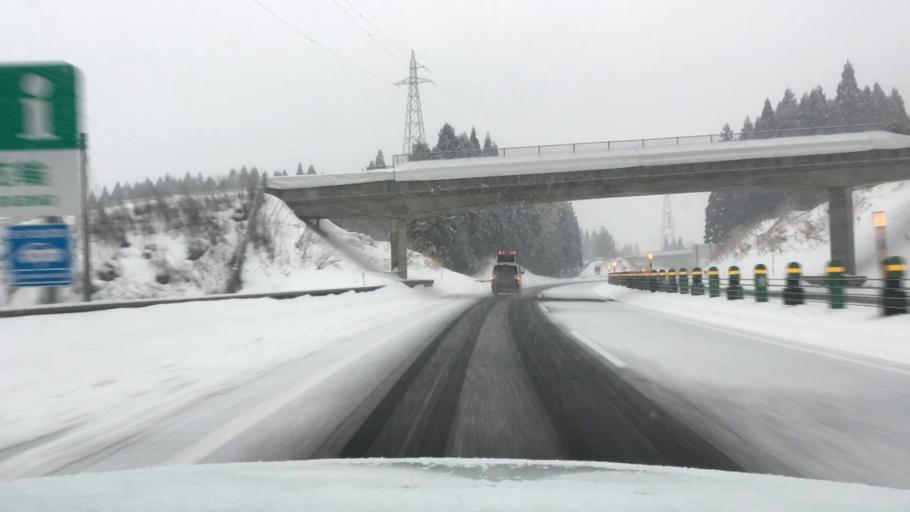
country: JP
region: Akita
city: Hanawa
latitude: 40.1677
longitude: 140.7996
